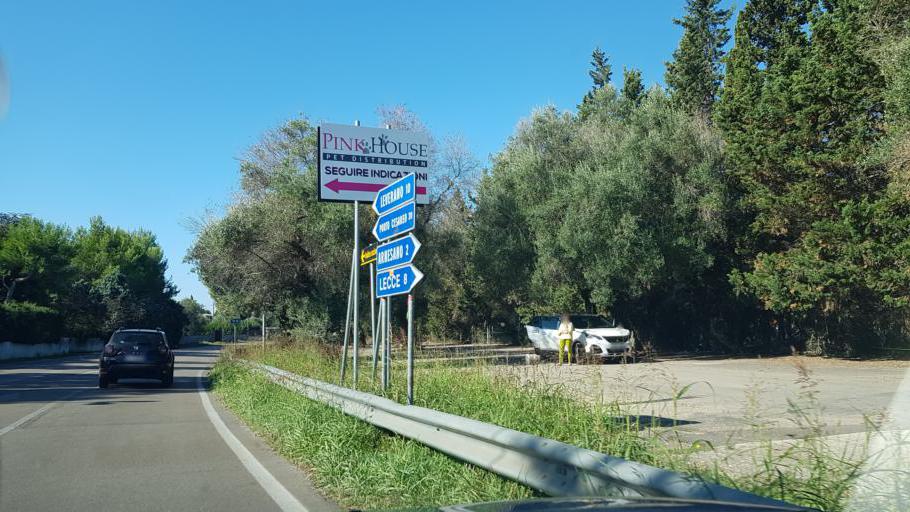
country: IT
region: Apulia
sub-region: Provincia di Lecce
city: Magliano
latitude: 40.3221
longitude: 18.0731
